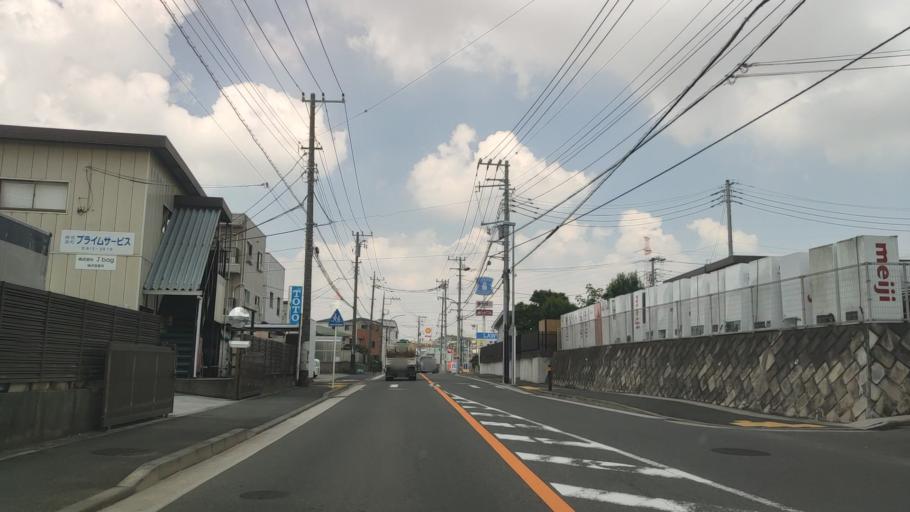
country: JP
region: Kanagawa
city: Minami-rinkan
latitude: 35.4287
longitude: 139.5155
